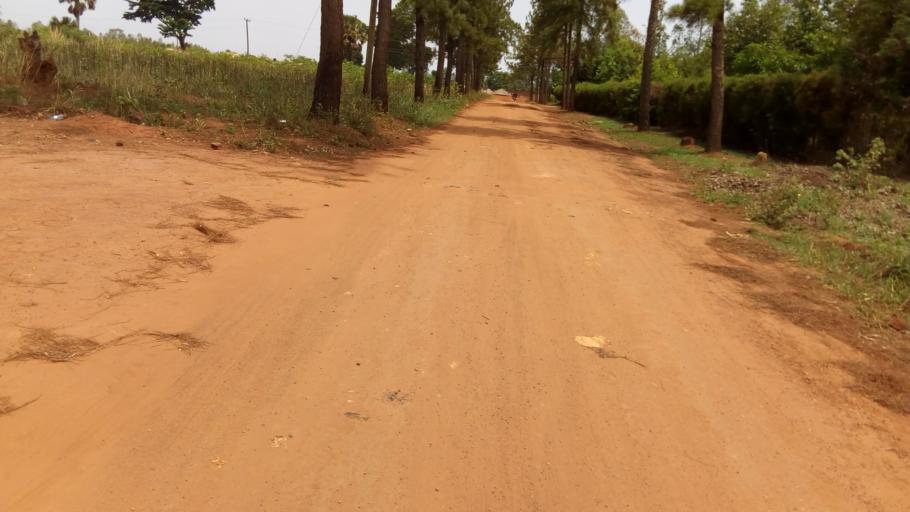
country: UG
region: Northern Region
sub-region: Gulu District
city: Gulu
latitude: 2.7729
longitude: 32.3192
